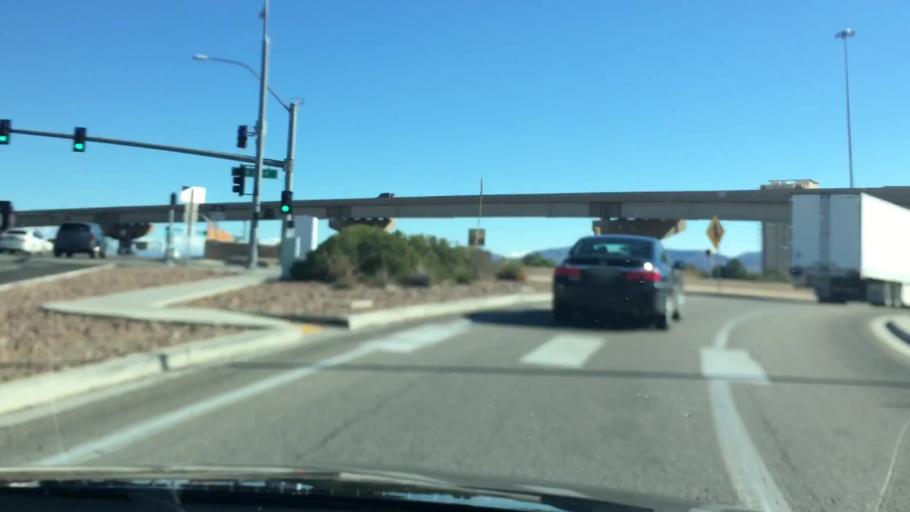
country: US
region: Nevada
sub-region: Clark County
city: Enterprise
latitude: 36.0432
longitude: -115.1818
